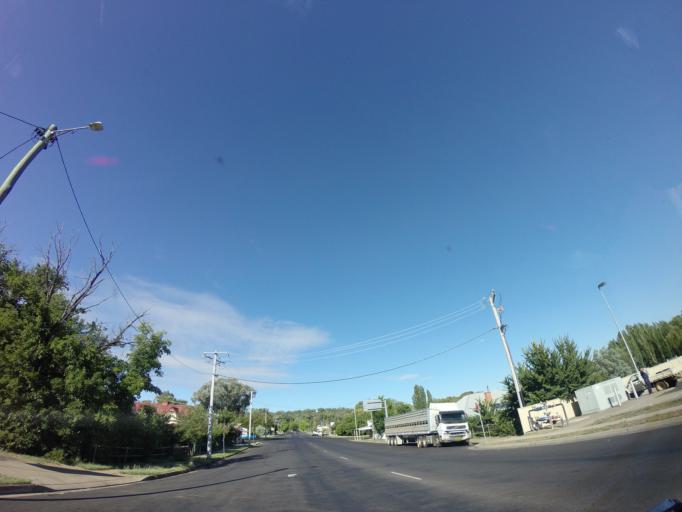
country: AU
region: New South Wales
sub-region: Warrumbungle Shire
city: Coonabarabran
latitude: -31.2739
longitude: 149.2759
